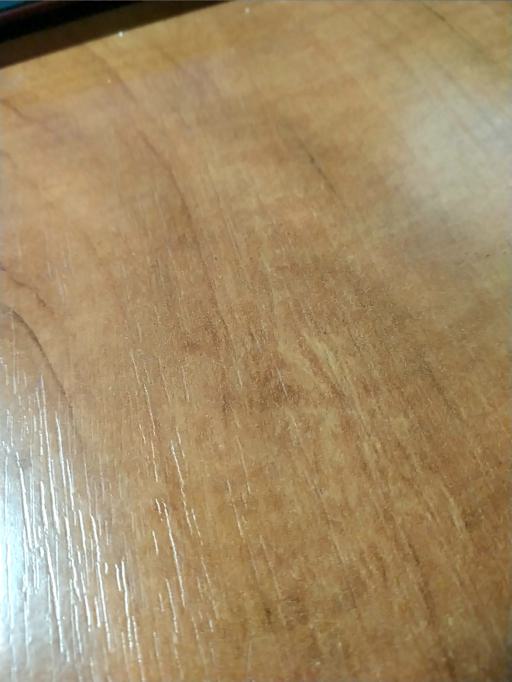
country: RU
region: Tverskaya
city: Vyshniy Volochek
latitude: 57.3511
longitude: 34.5862
